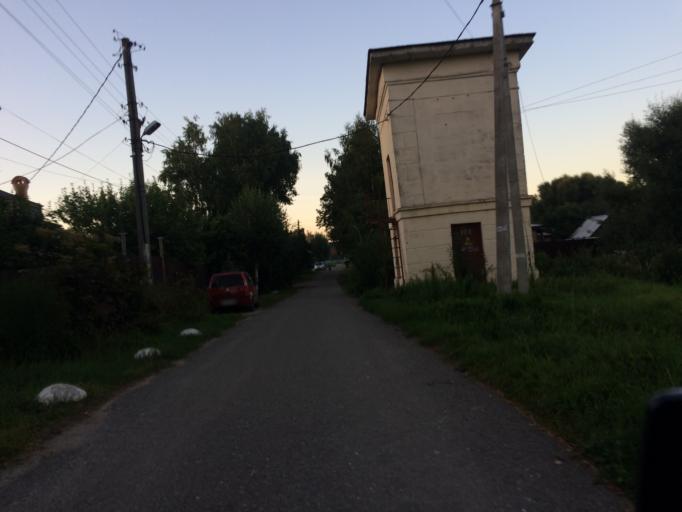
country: RU
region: Mariy-El
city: Yoshkar-Ola
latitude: 56.6419
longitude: 47.9066
